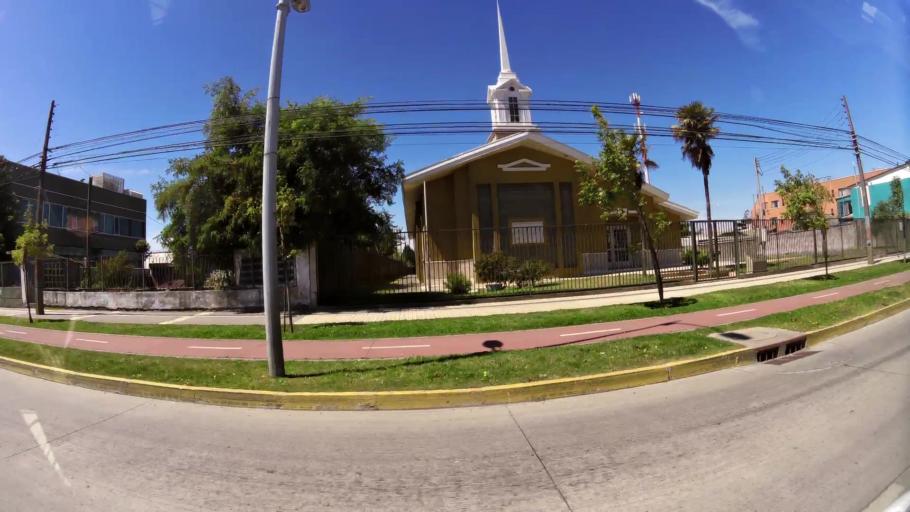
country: CL
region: Biobio
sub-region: Provincia de Concepcion
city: Talcahuano
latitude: -36.7509
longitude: -73.0929
